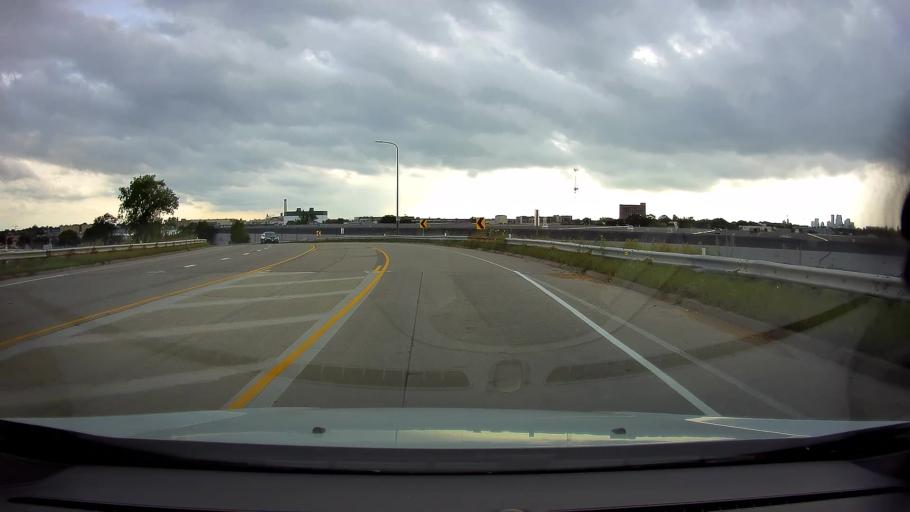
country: US
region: Minnesota
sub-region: Ramsey County
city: Falcon Heights
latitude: 44.9680
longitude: -93.1851
